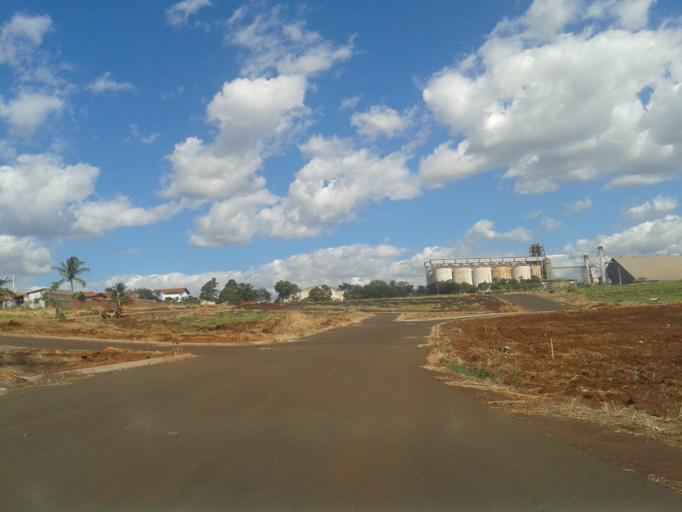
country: BR
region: Minas Gerais
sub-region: Capinopolis
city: Capinopolis
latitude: -18.6918
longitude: -49.5699
